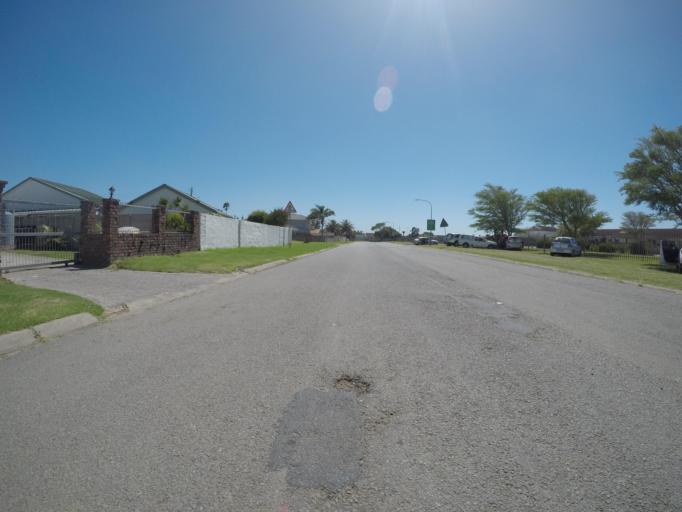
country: ZA
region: Eastern Cape
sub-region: Buffalo City Metropolitan Municipality
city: East London
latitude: -32.9713
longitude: 27.9496
